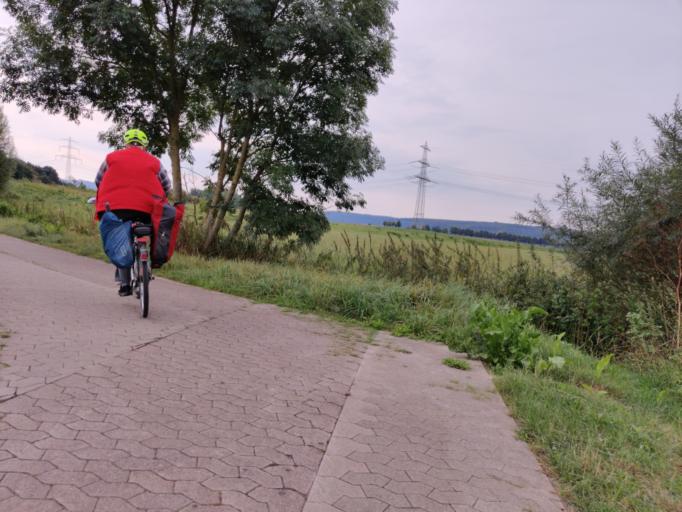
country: DE
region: Lower Saxony
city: Hehlen
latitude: 52.0279
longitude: 9.4308
